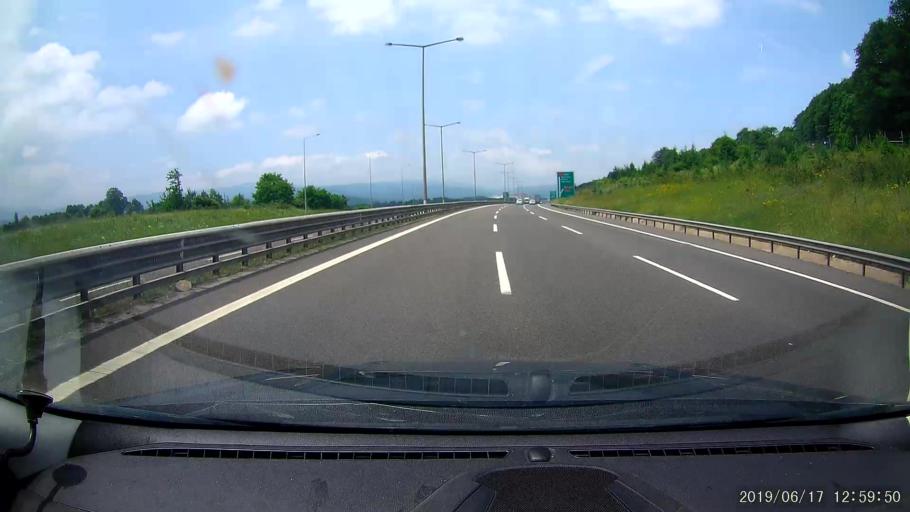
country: TR
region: Bolu
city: Bolu
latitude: 40.7205
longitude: 31.4865
